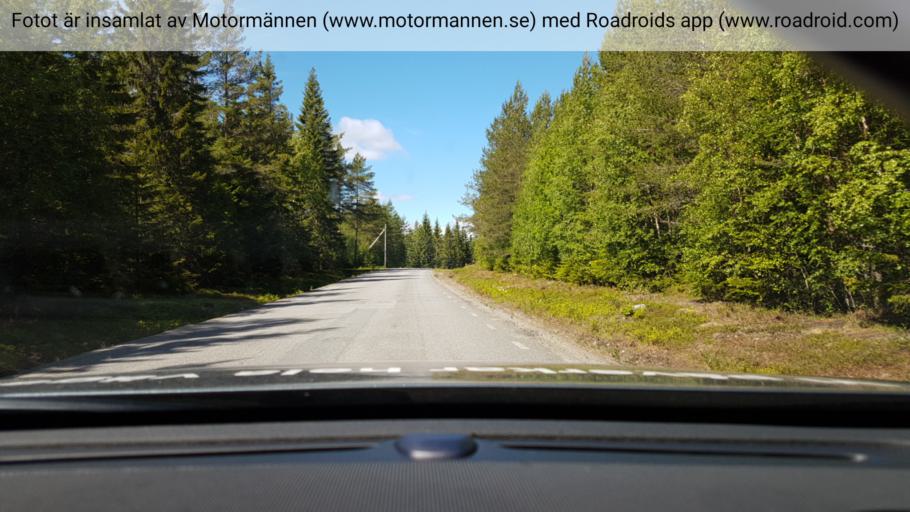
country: SE
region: Vaesterbotten
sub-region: Skelleftea Kommun
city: Burea
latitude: 64.4555
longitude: 21.4281
